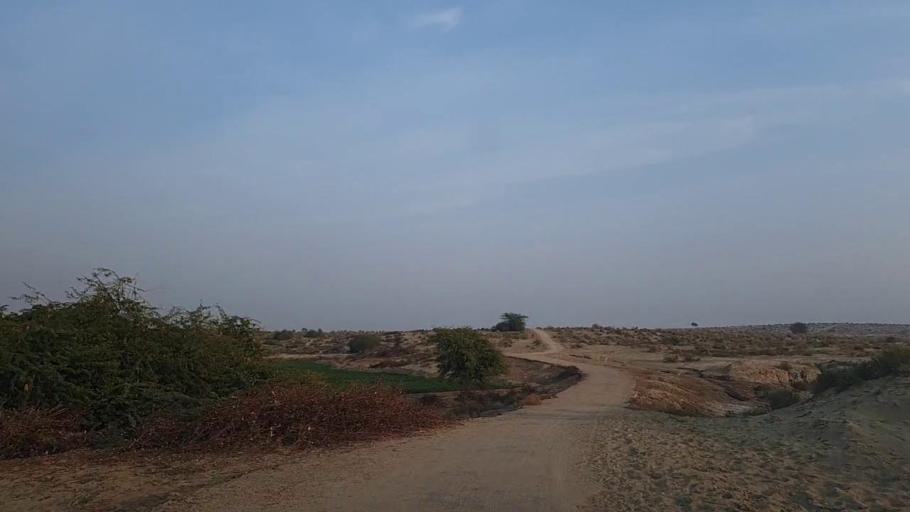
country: PK
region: Sindh
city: Jam Sahib
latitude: 26.4086
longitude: 68.6078
